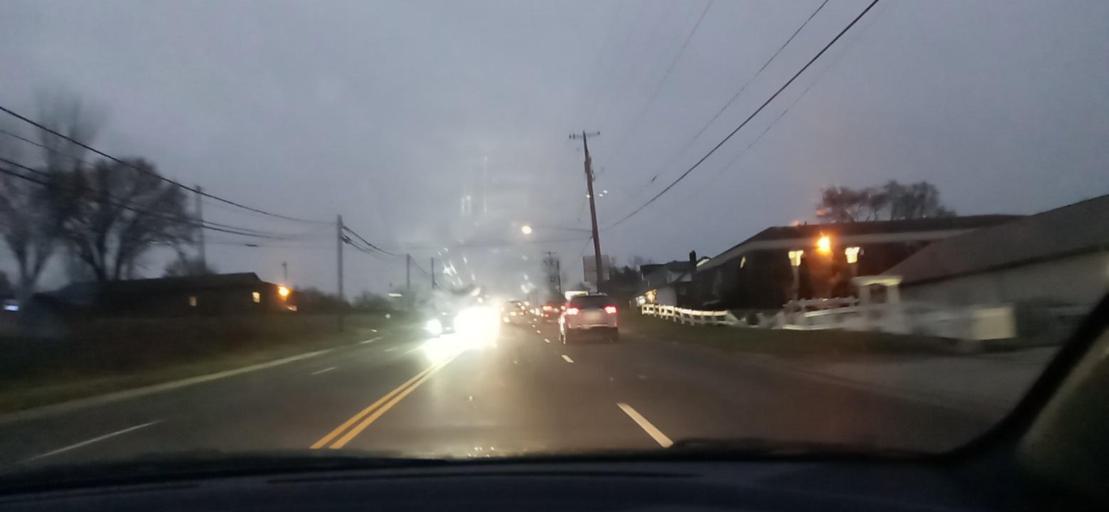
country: US
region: Ohio
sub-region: Summit County
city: Portage Lakes
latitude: 41.0033
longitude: -81.4920
